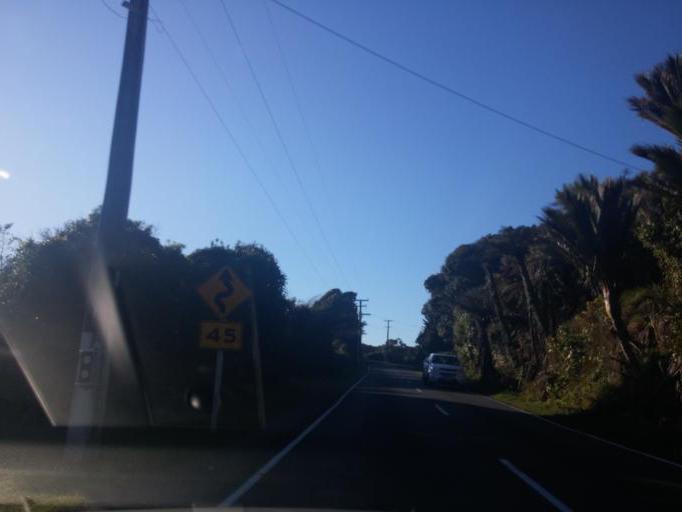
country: NZ
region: West Coast
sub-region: Grey District
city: Greymouth
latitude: -42.1024
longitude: 171.3401
